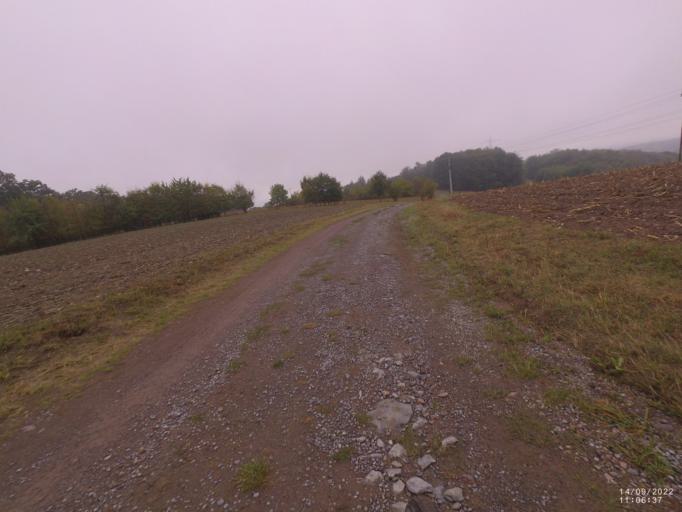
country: DE
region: Bavaria
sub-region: Regierungsbezirk Unterfranken
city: Johannesberg
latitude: 50.0179
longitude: 9.1320
